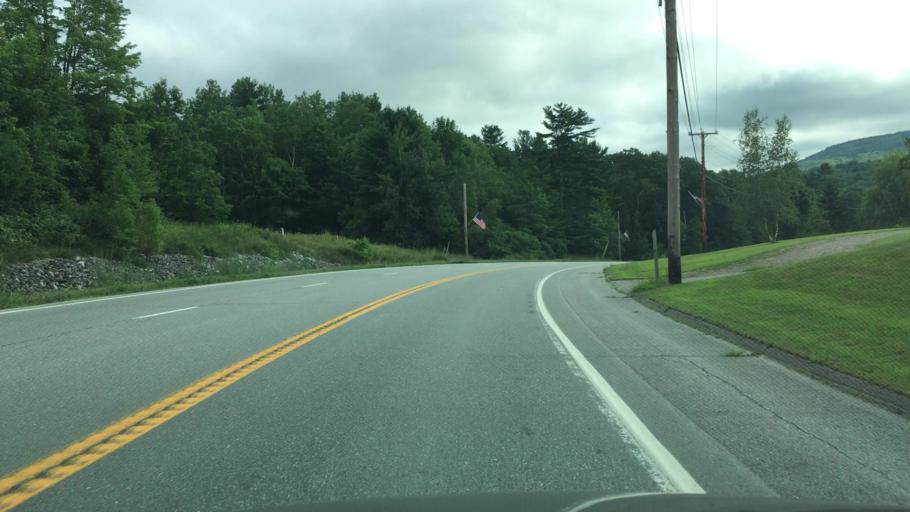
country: US
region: Maine
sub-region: Waldo County
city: Frankfort
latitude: 44.6135
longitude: -68.8694
